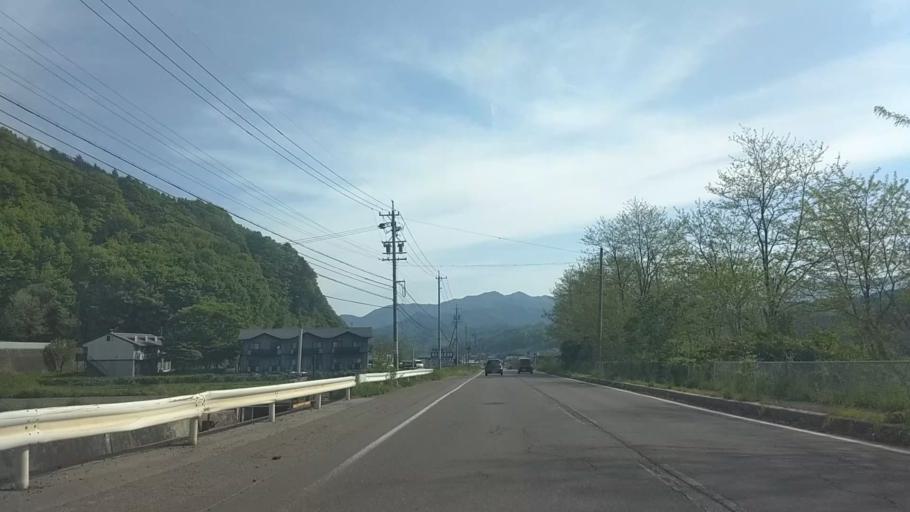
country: JP
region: Nagano
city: Saku
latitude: 36.0639
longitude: 138.4713
